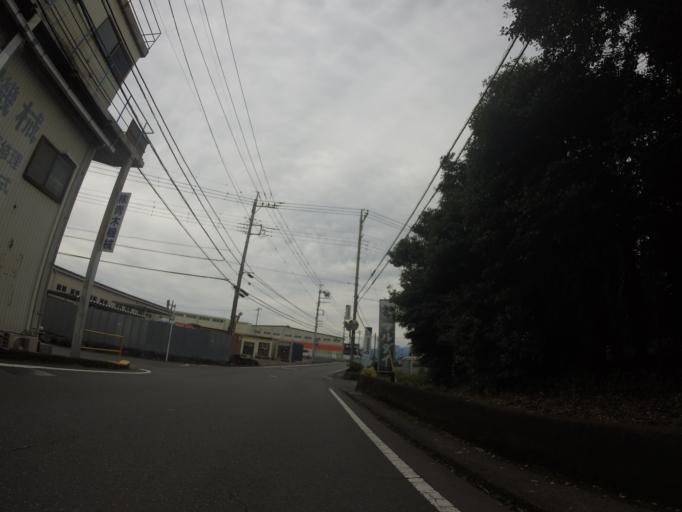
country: JP
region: Shizuoka
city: Fuji
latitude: 35.1977
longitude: 138.6765
